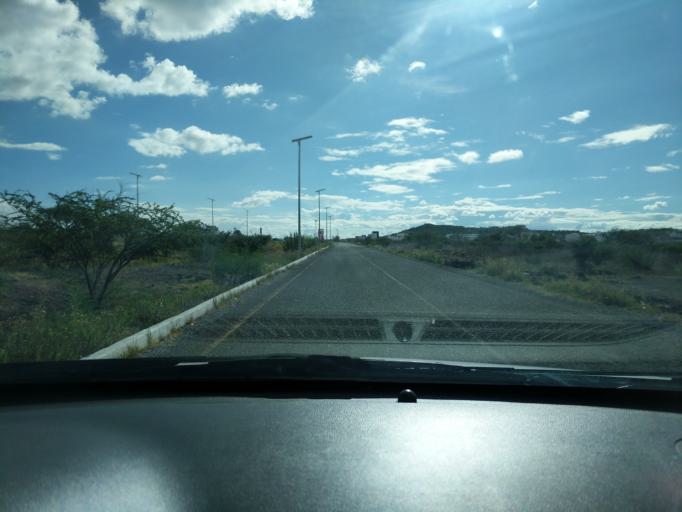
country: MX
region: Queretaro
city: La Canada
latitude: 20.5970
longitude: -100.3035
